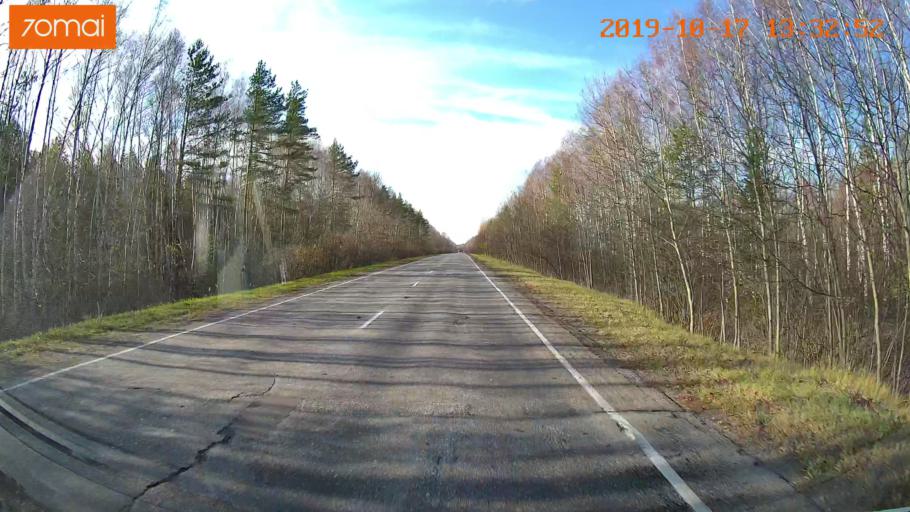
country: RU
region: Vladimir
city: Velikodvorskiy
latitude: 55.1394
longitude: 40.7549
